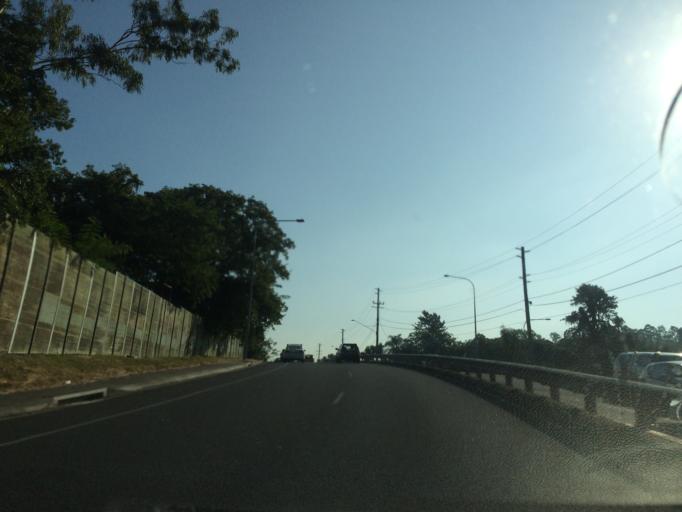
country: AU
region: Queensland
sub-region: Brisbane
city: Kenmore Hills
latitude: -27.5148
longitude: 152.9288
